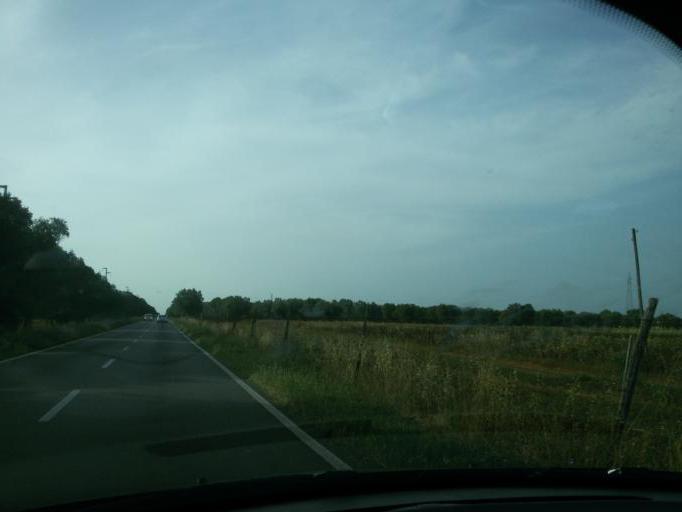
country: IT
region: Apulia
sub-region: Provincia di Brindisi
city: San Pancrazio Salentino
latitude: 40.3566
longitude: 17.8440
